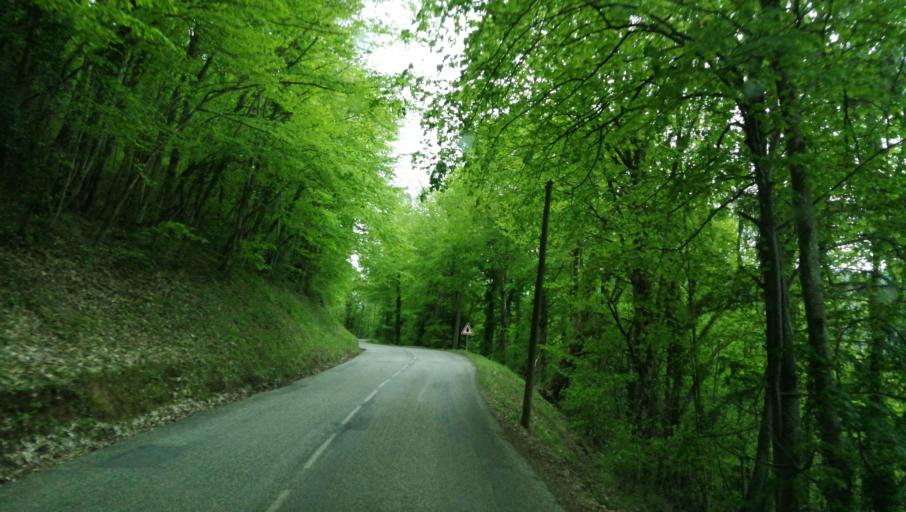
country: FR
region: Rhone-Alpes
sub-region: Departement de la Drome
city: Saint-Jean-en-Royans
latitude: 45.0072
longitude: 5.3003
